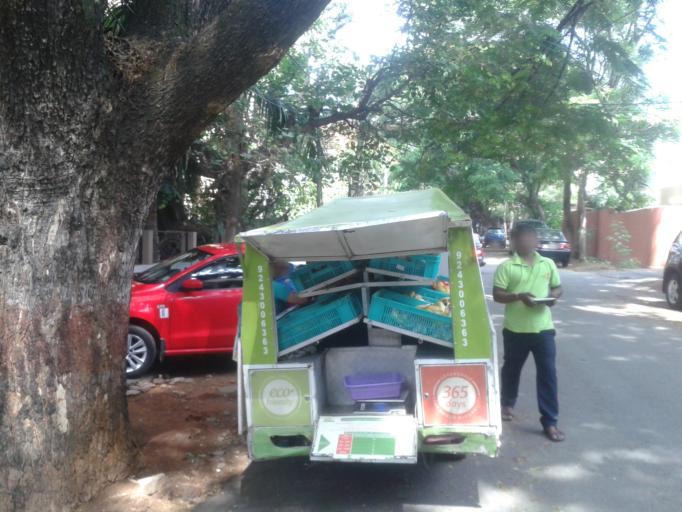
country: IN
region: Karnataka
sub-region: Bangalore Urban
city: Bangalore
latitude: 12.9756
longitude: 77.6430
